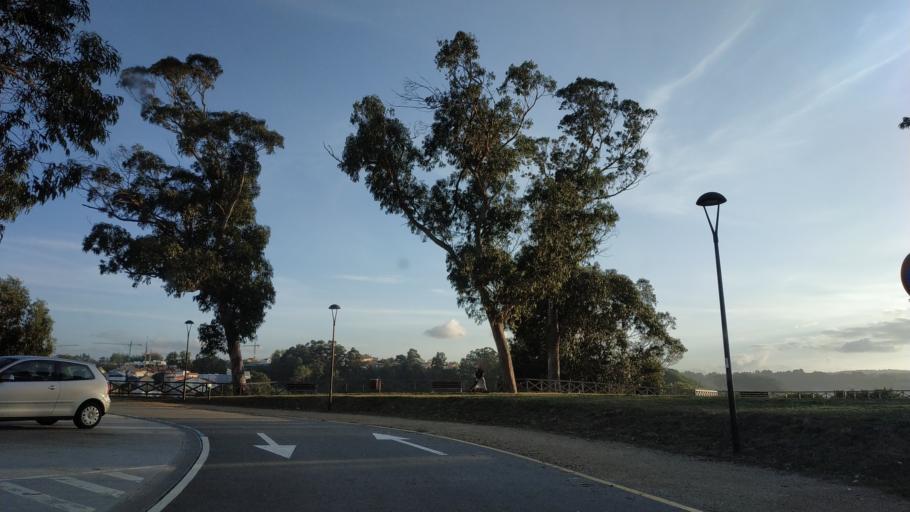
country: ES
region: Galicia
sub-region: Provincia da Coruna
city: Oleiros
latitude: 43.3513
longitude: -8.3478
